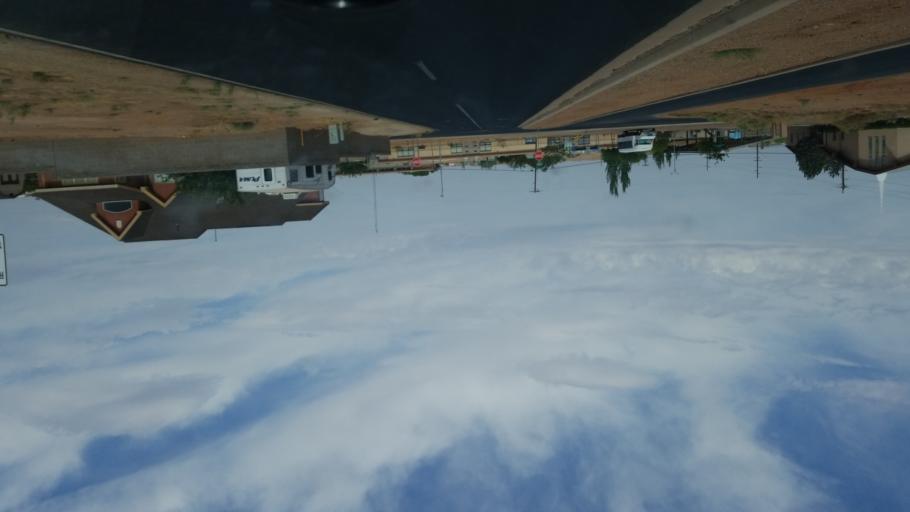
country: US
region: Arizona
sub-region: Navajo County
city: Winslow
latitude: 35.0397
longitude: -110.7233
